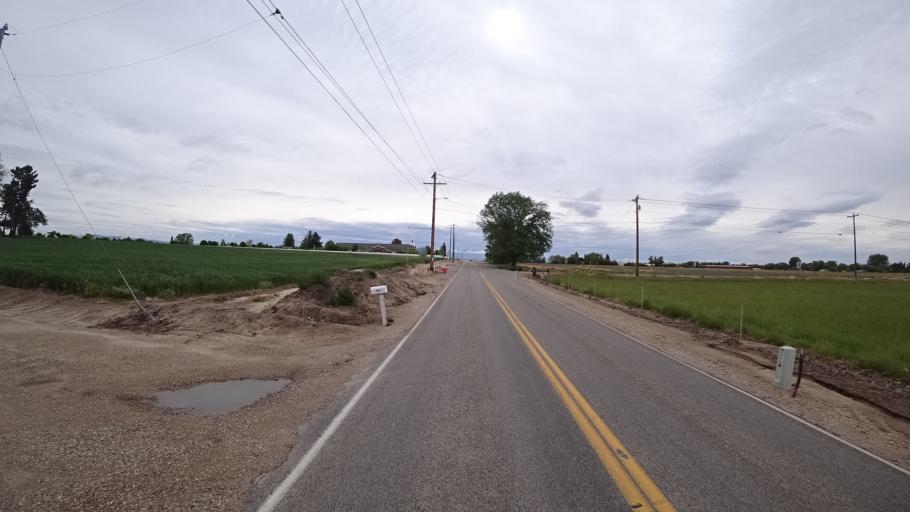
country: US
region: Idaho
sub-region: Ada County
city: Star
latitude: 43.7065
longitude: -116.4740
